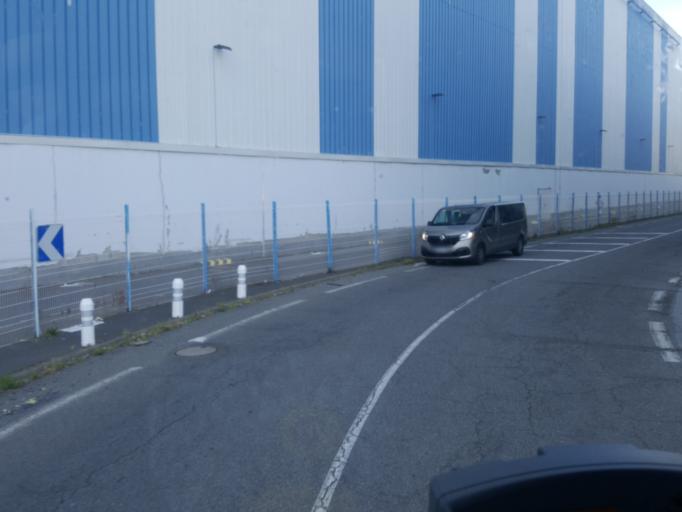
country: FR
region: Pays de la Loire
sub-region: Departement de la Loire-Atlantique
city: Saint-Nazaire
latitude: 47.2849
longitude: -2.1953
